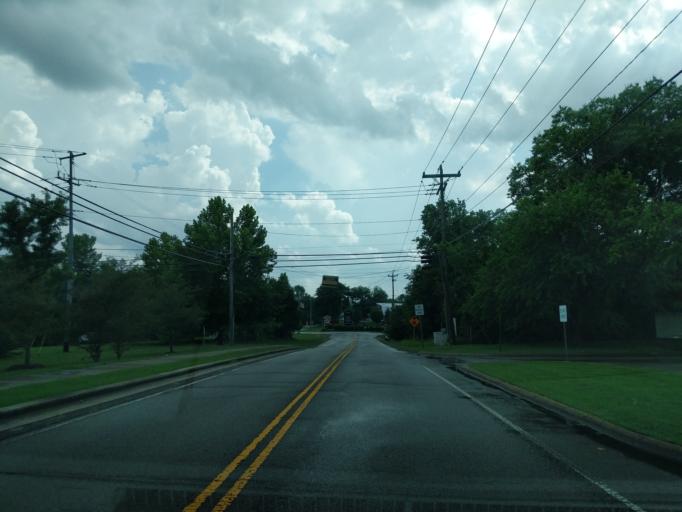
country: US
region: Tennessee
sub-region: Cheatham County
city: Pegram
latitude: 36.0447
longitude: -86.9579
